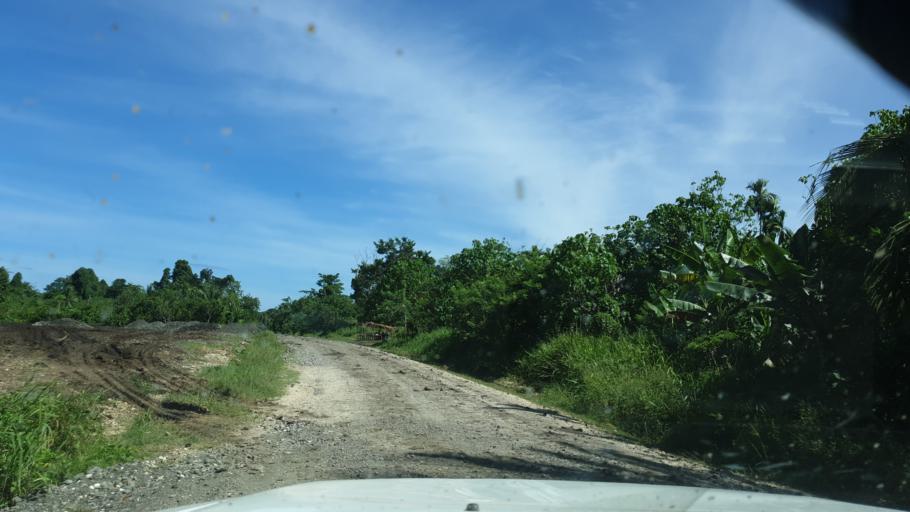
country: PG
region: Madang
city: Madang
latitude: -4.6739
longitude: 145.5857
